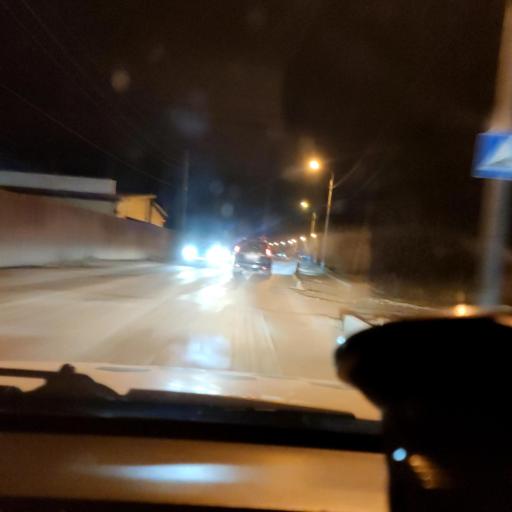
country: RU
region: Perm
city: Kondratovo
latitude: 57.9625
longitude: 56.1228
